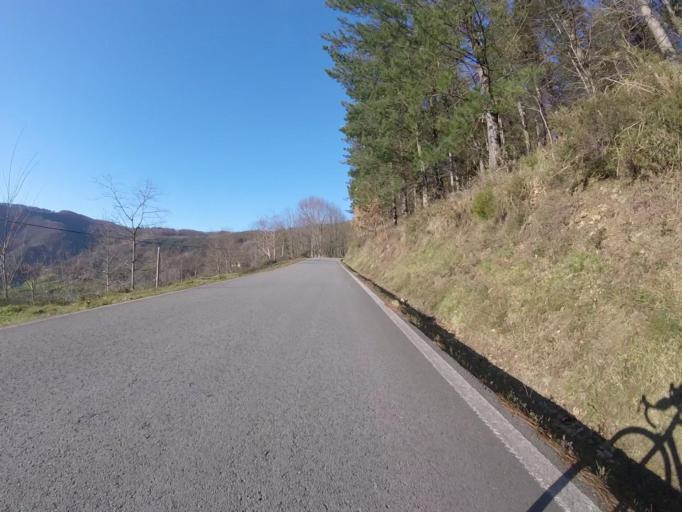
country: ES
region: Navarre
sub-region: Provincia de Navarra
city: Lesaka
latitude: 43.2611
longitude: -1.7372
